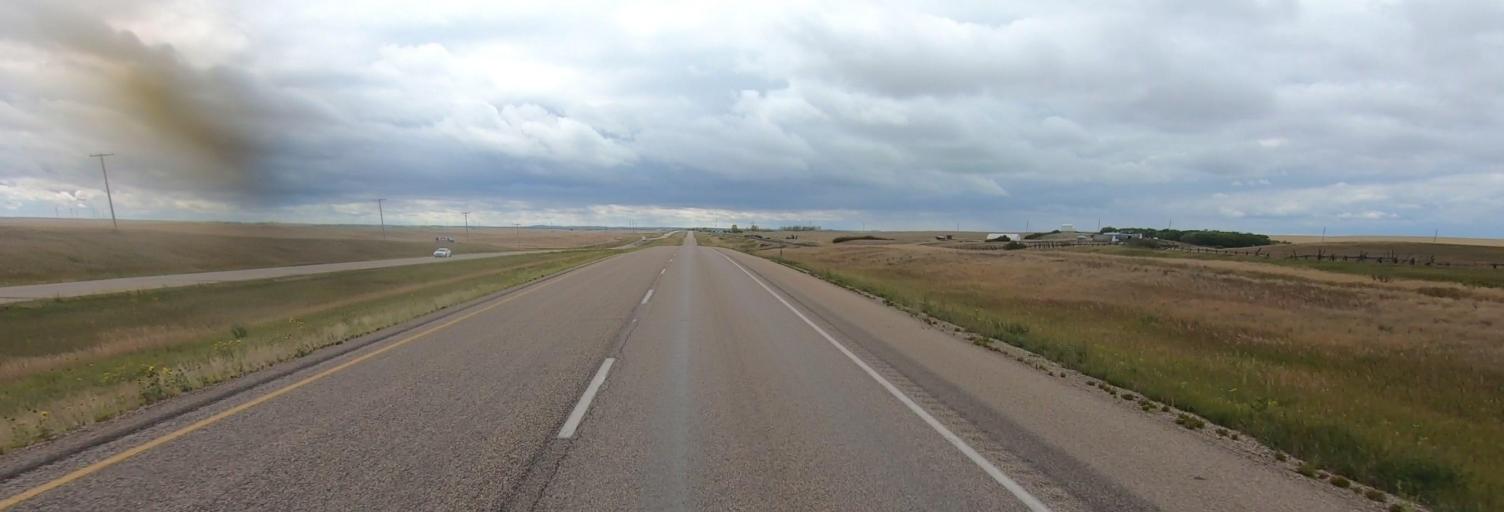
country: CA
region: Saskatchewan
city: Gravelbourg
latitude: 50.4285
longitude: -106.9263
